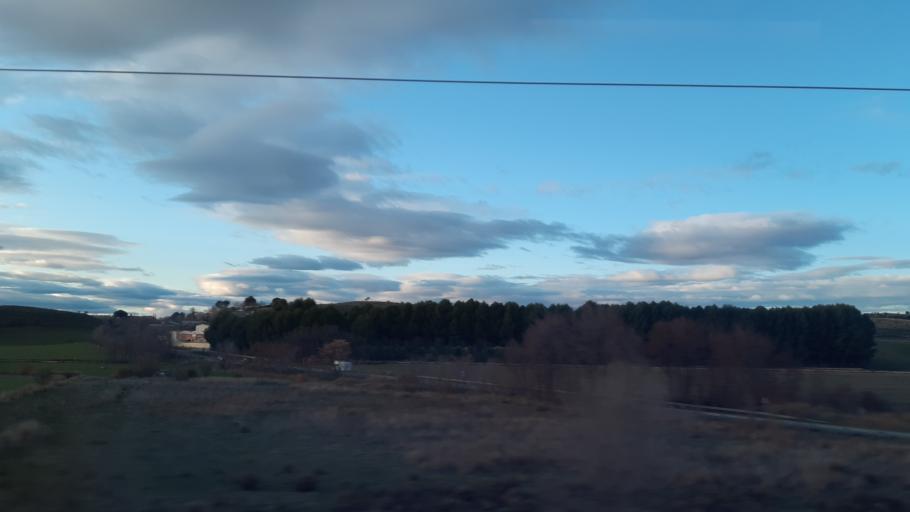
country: ES
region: Madrid
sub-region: Provincia de Madrid
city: Villalbilla
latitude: 40.4478
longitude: -3.3319
